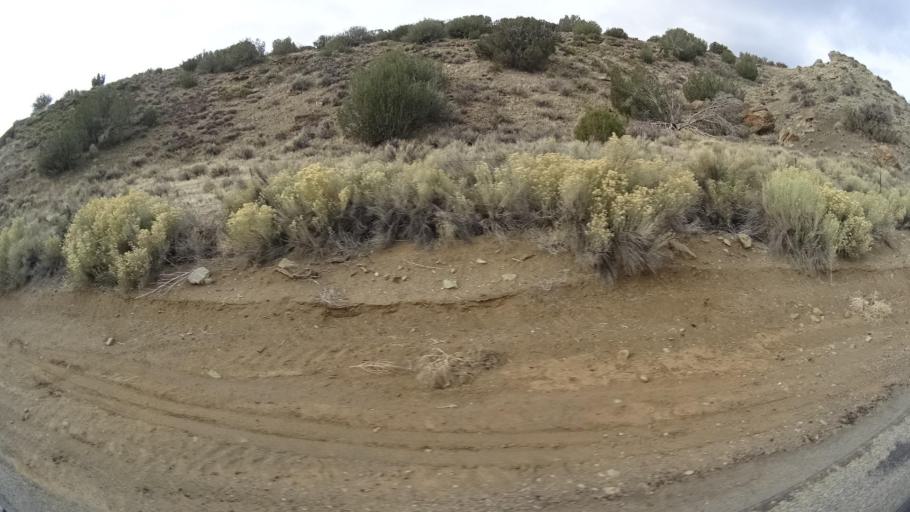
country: US
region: California
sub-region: Kern County
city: Tehachapi
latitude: 35.1580
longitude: -118.3226
